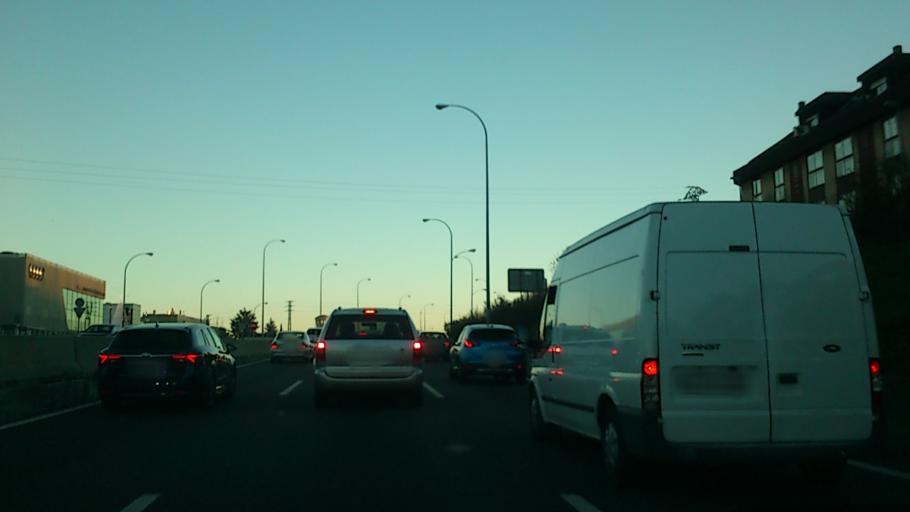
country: ES
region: Madrid
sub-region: Provincia de Madrid
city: Las Rozas de Madrid
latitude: 40.4910
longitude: -3.8671
